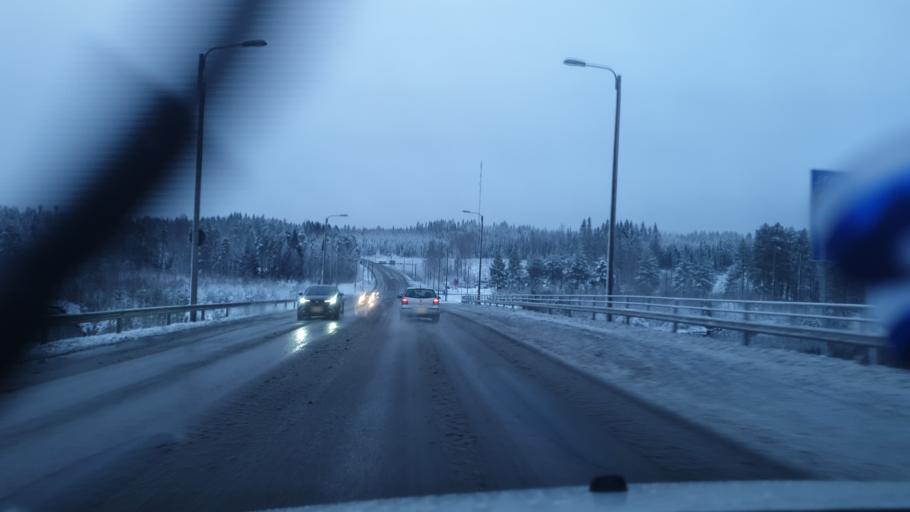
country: FI
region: Central Finland
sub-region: Saarijaervi-Viitasaari
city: Viitasaari
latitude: 63.0422
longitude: 25.8158
